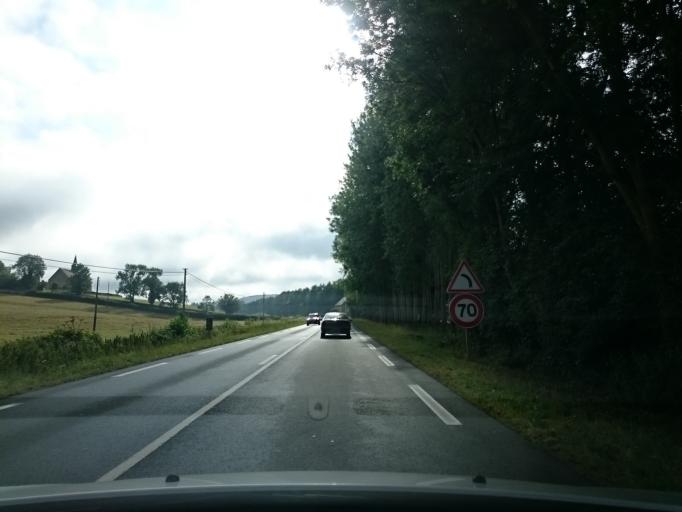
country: FR
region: Lower Normandy
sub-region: Departement du Calvados
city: Cambremer
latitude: 49.1145
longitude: 0.0474
